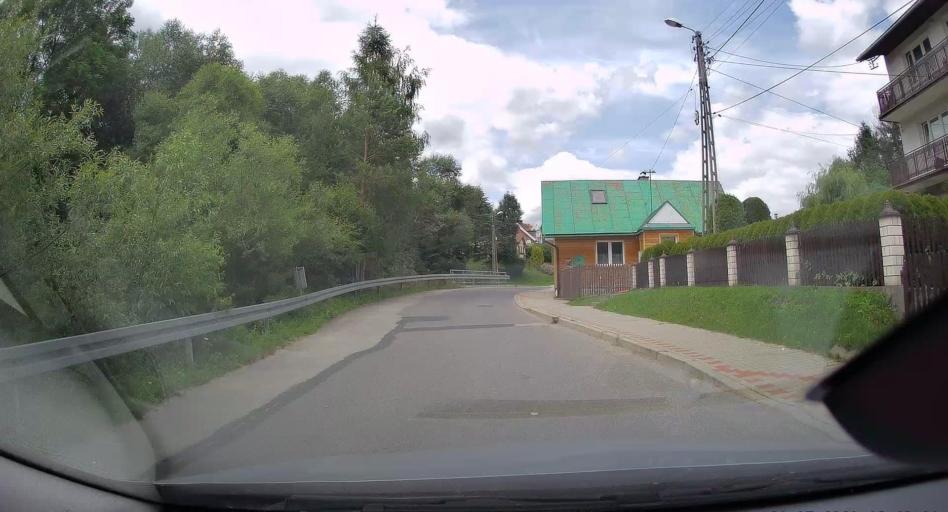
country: PL
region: Lesser Poland Voivodeship
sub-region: Powiat nowosadecki
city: Muszyna
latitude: 49.3719
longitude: 20.8884
